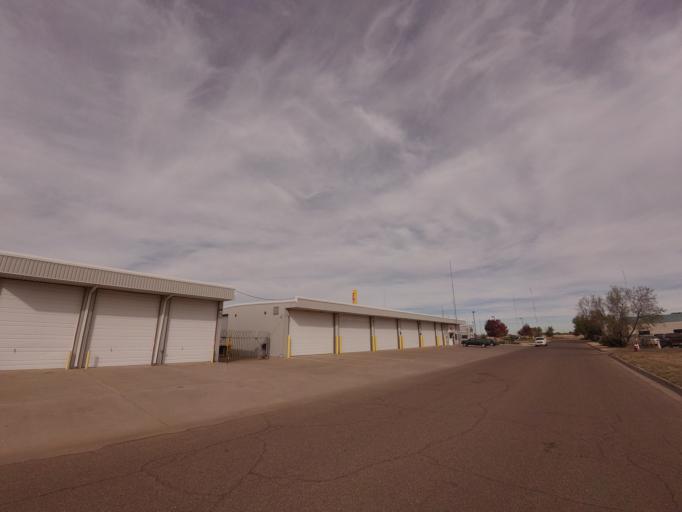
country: US
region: New Mexico
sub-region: Curry County
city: Clovis
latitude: 34.4324
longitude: -103.2101
